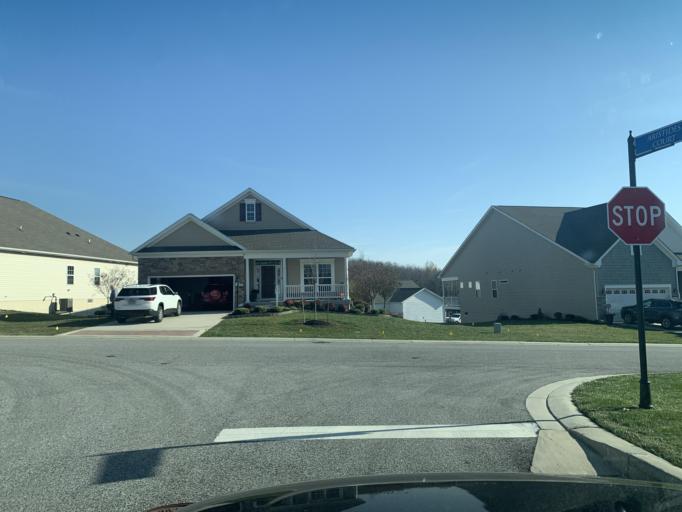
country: US
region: Maryland
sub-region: Harford County
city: Havre de Grace
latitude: 39.5418
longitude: -76.1194
